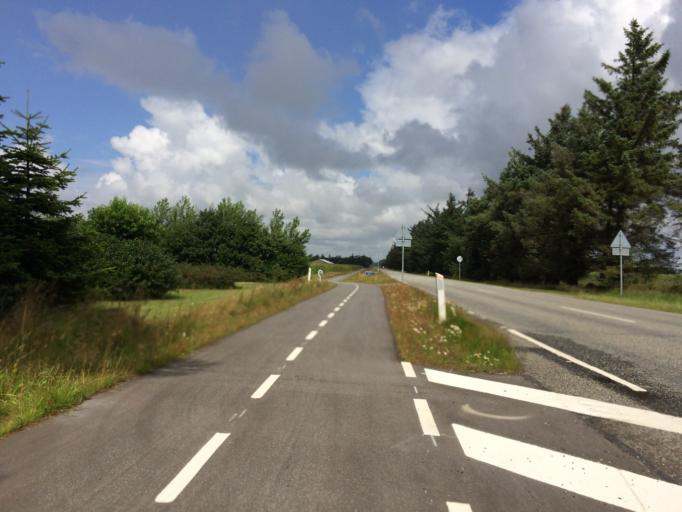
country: DK
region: Central Jutland
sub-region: Holstebro Kommune
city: Ulfborg
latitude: 56.3022
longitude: 8.3387
